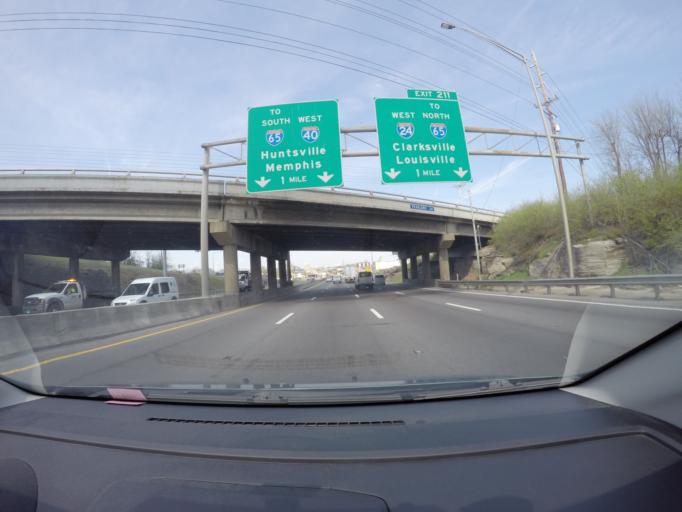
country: US
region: Tennessee
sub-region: Davidson County
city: Nashville
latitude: 36.1471
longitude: -86.7434
